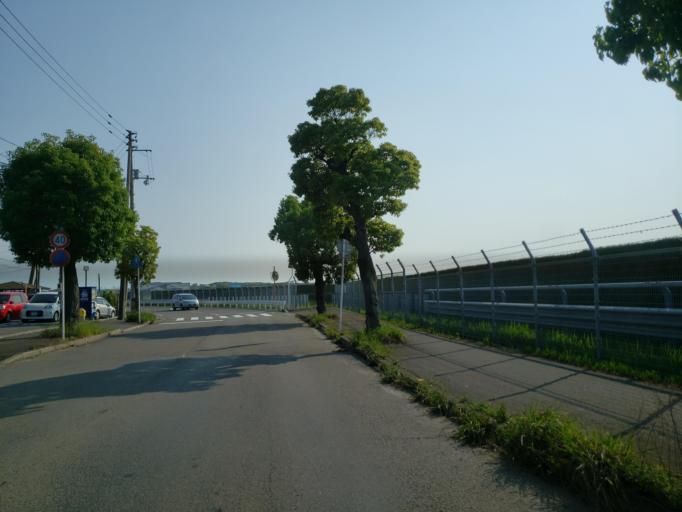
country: JP
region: Ehime
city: Masaki-cho
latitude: 33.8271
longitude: 132.7056
